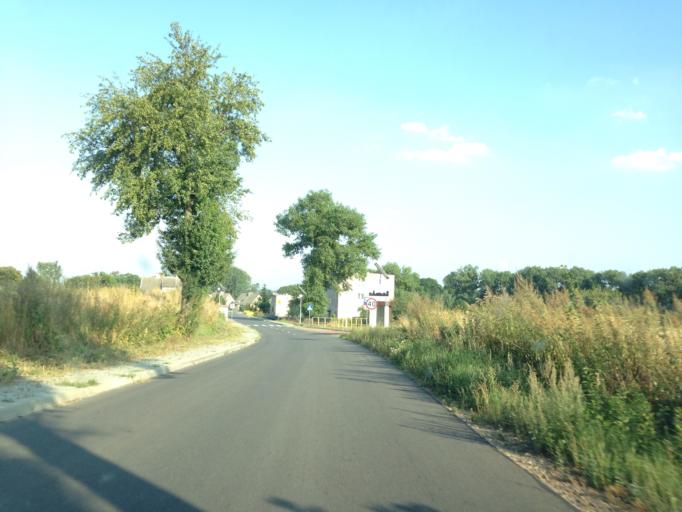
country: PL
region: Warmian-Masurian Voivodeship
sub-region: Powiat nowomiejski
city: Biskupiec
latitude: 53.4170
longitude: 19.3337
